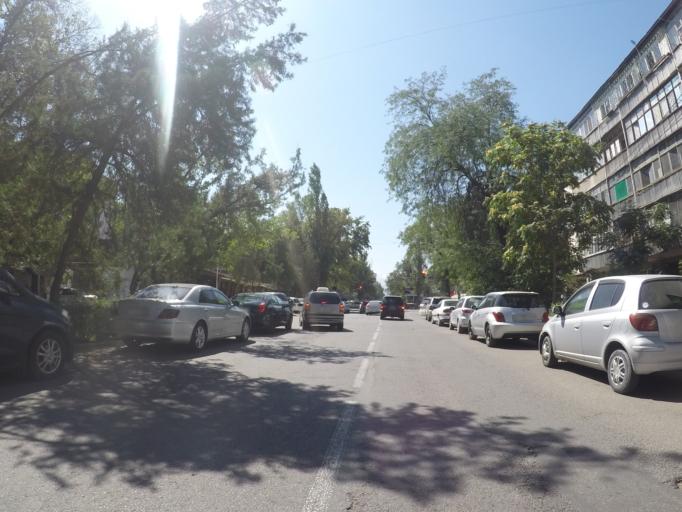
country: KG
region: Chuy
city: Bishkek
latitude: 42.8773
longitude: 74.5918
